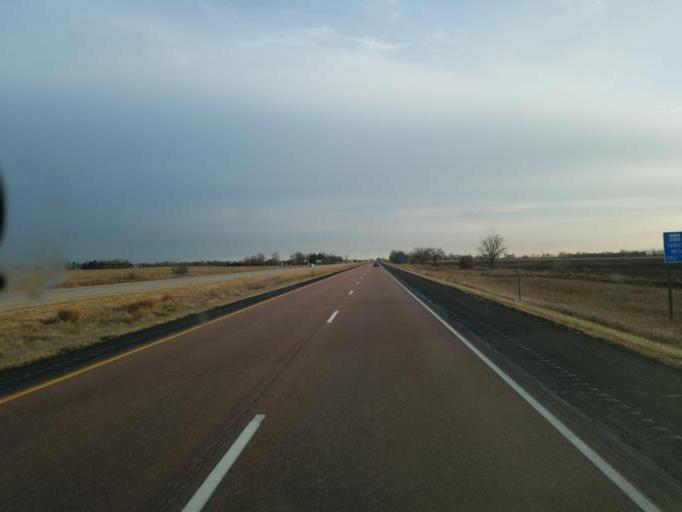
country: US
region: Iowa
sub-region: Monona County
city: Onawa
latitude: 42.0038
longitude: -96.1157
